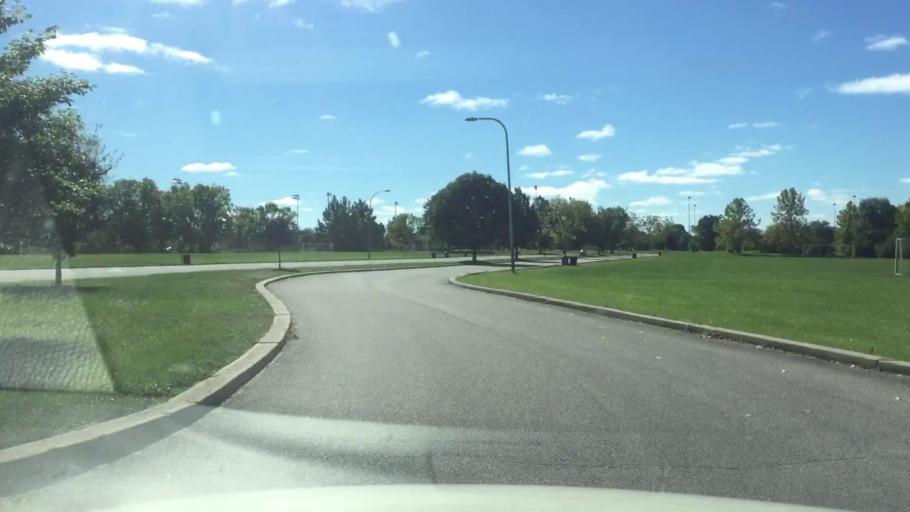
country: US
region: Missouri
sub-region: Boone County
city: Columbia
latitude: 38.9751
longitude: -92.3635
